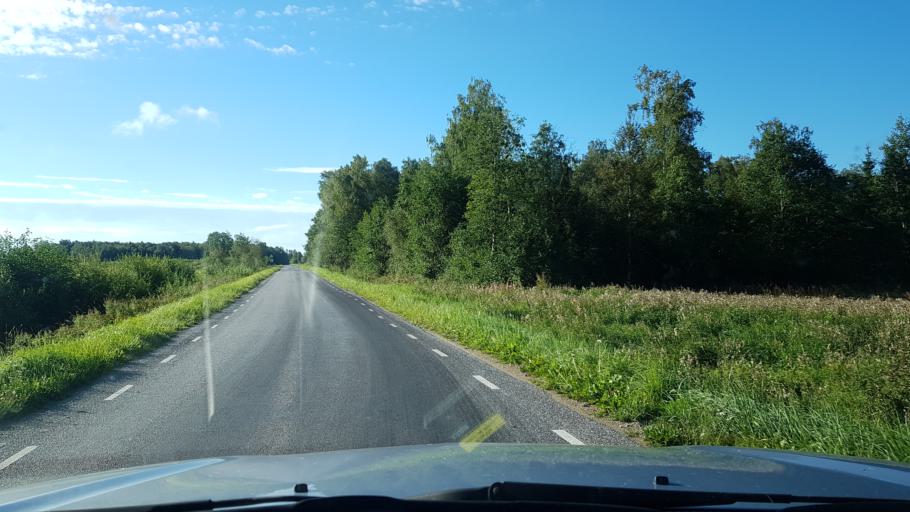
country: EE
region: Harju
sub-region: Rae vald
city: Vaida
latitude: 59.3099
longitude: 24.9240
